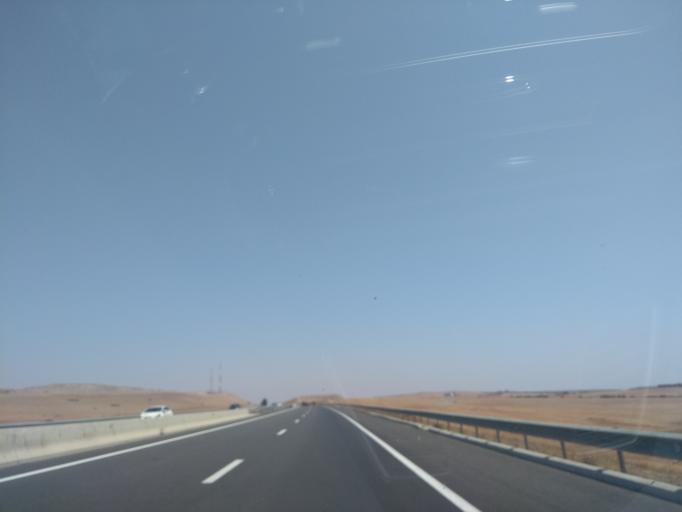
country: MA
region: Marrakech-Tensift-Al Haouz
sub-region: Kelaa-Des-Sraghna
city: Sidi Abdallah
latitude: 32.3013
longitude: -7.9593
